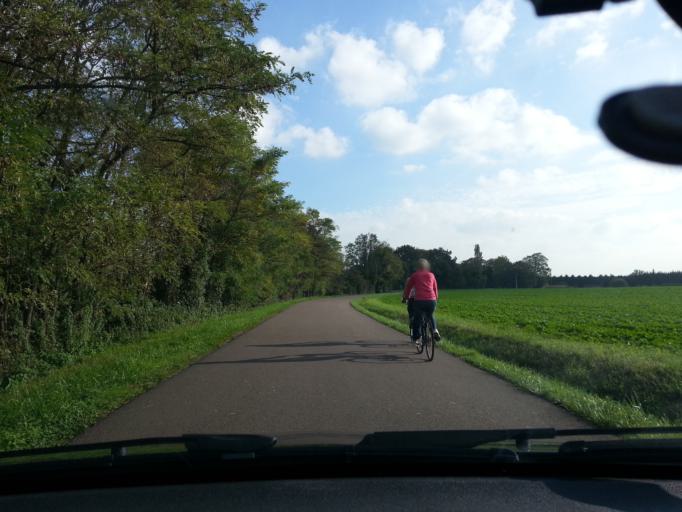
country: FR
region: Bourgogne
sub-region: Departement de Saone-et-Loire
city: Dracy-le-Fort
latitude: 46.7877
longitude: 4.7806
